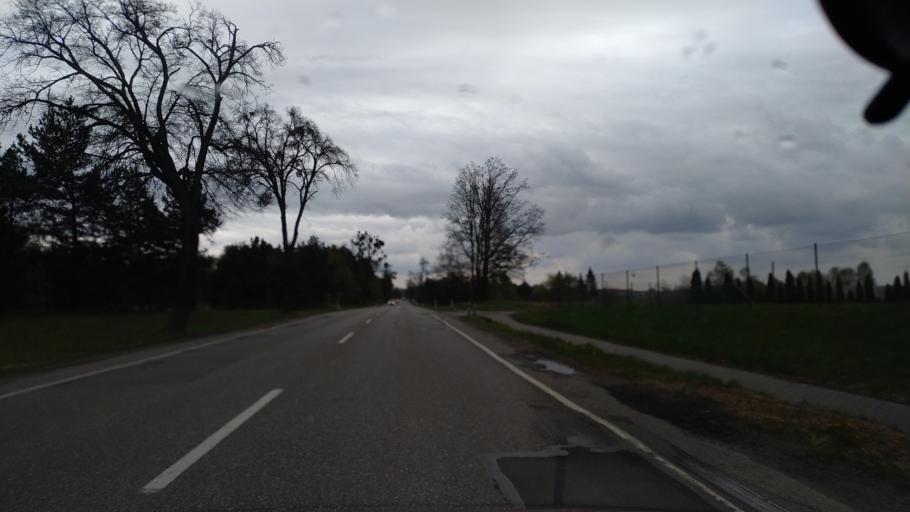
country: PL
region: Pomeranian Voivodeship
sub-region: Powiat tczewski
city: Pelplin
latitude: 54.0280
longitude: 18.6452
